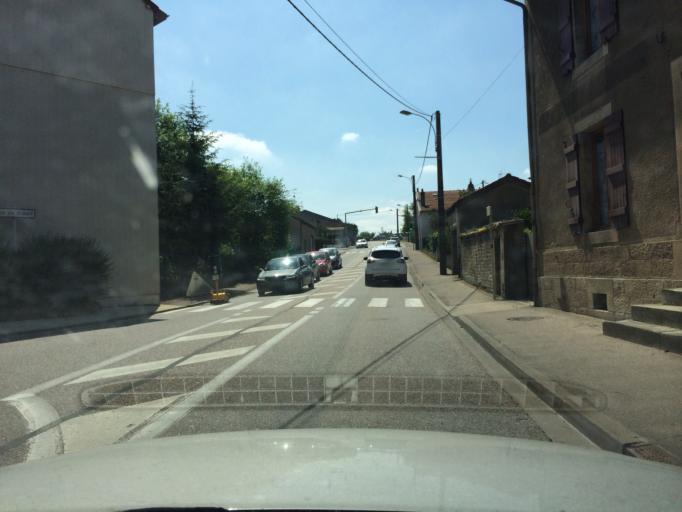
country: FR
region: Lorraine
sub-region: Departement de la Meuse
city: Commercy
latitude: 48.7577
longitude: 5.5847
